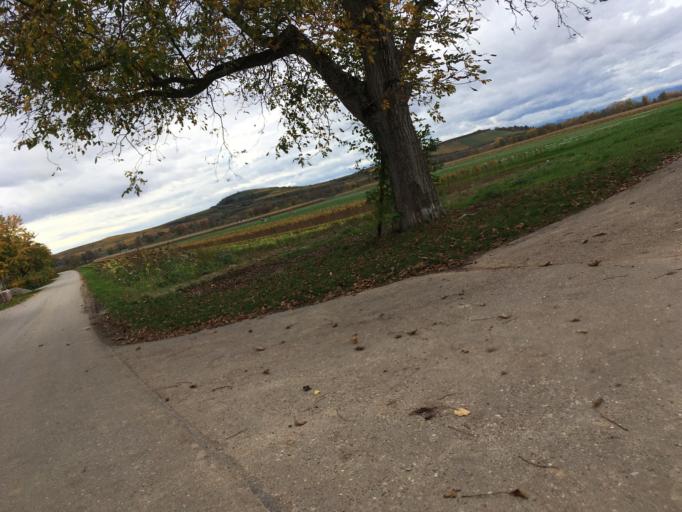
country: DE
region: Baden-Wuerttemberg
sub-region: Freiburg Region
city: Sasbach
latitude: 48.1401
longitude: 7.6408
